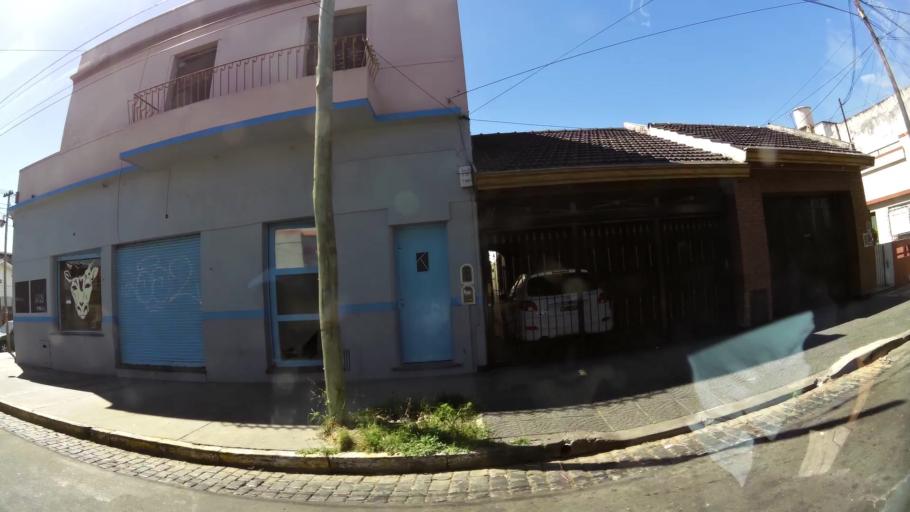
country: AR
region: Buenos Aires
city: Caseros
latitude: -34.5843
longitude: -58.5474
